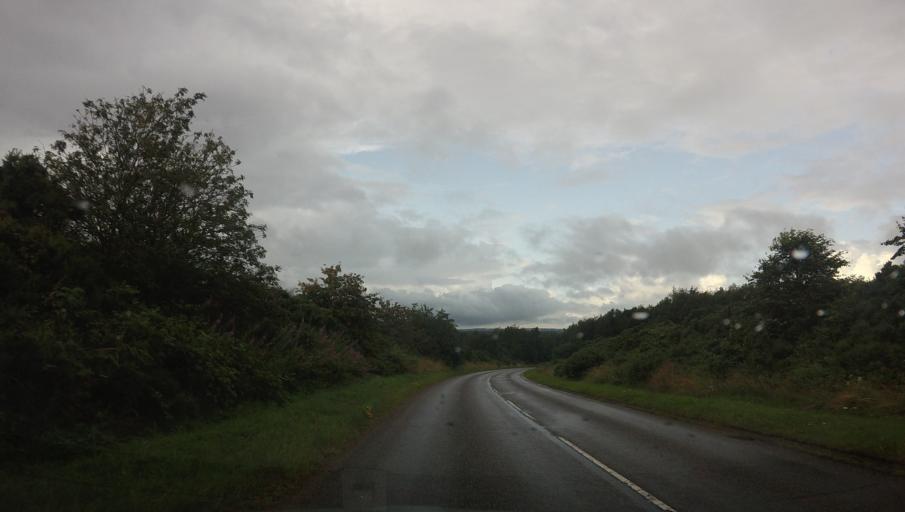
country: GB
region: Scotland
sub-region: Aberdeenshire
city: Banchory
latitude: 57.0433
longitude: -2.4175
